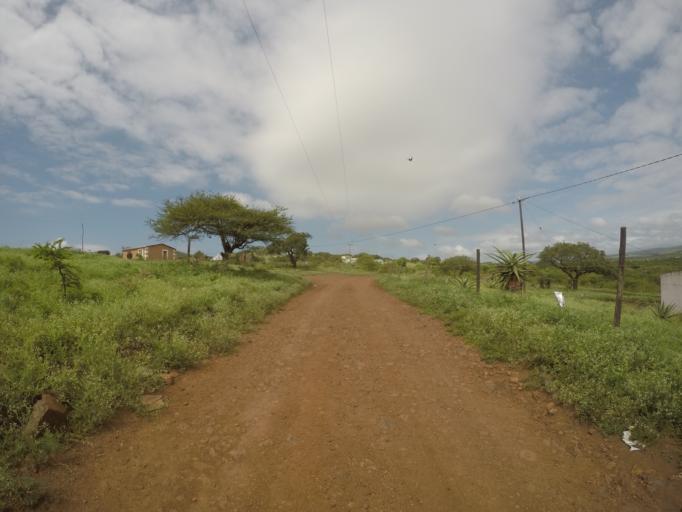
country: ZA
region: KwaZulu-Natal
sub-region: uThungulu District Municipality
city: Empangeni
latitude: -28.6209
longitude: 31.8718
